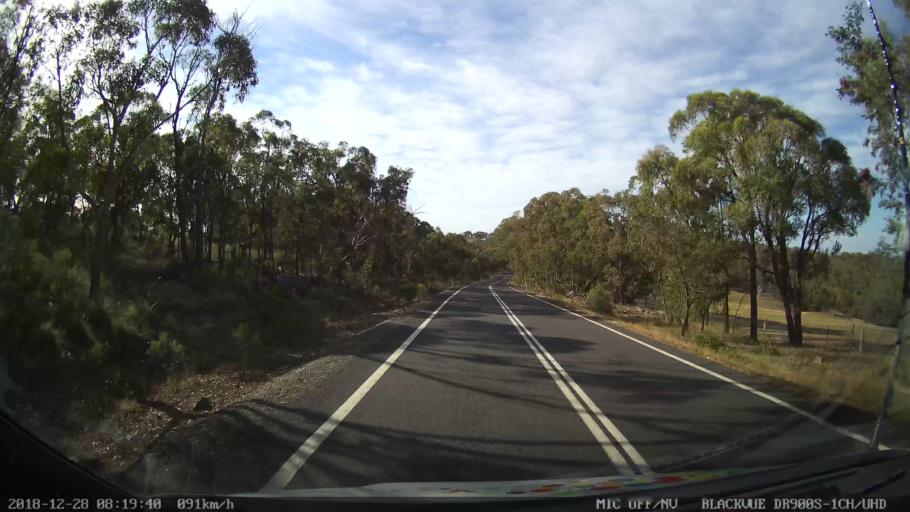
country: AU
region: New South Wales
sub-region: Blayney
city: Blayney
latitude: -33.8621
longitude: 149.3519
